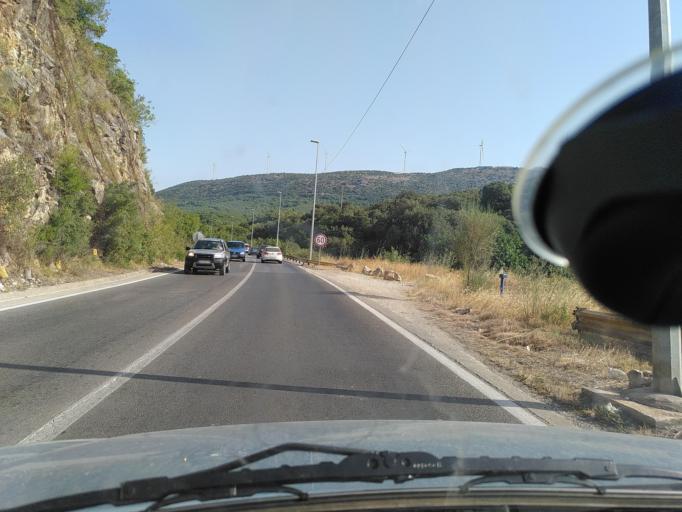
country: ME
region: Ulcinj
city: Ulcinj
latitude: 41.9628
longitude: 19.1915
